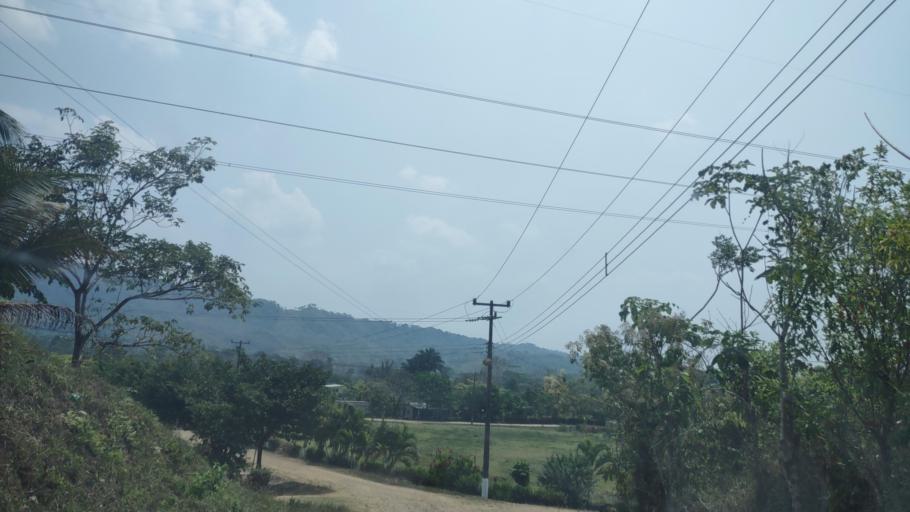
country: MX
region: Tabasco
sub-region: Huimanguillo
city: Francisco Rueda
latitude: 17.4947
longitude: -93.8425
